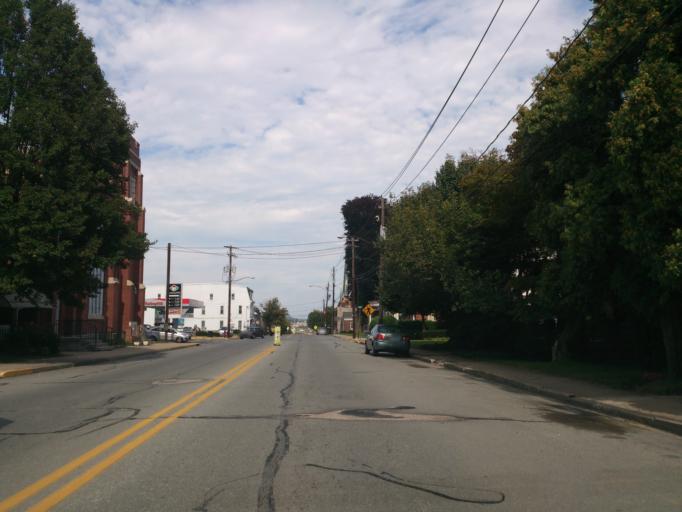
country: US
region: Pennsylvania
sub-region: York County
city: Wrightsville
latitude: 40.0247
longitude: -76.5346
